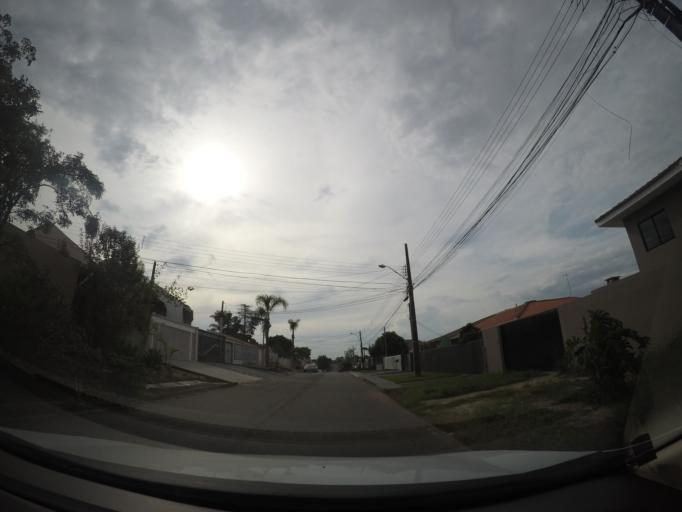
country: BR
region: Parana
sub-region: Sao Jose Dos Pinhais
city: Sao Jose dos Pinhais
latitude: -25.5097
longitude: -49.2606
